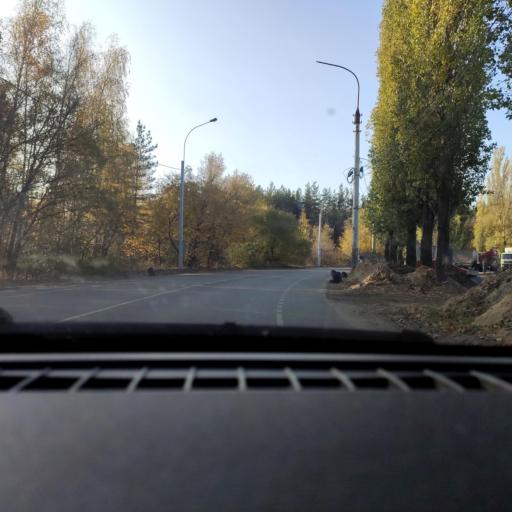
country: RU
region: Voronezj
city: Somovo
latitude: 51.7030
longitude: 39.2903
